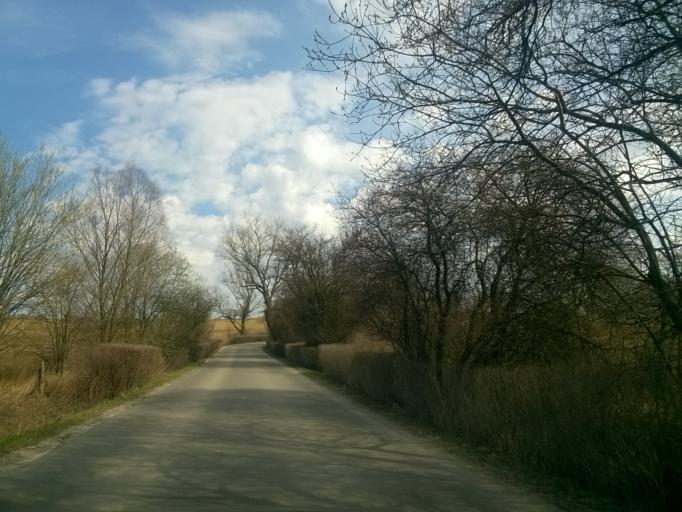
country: PL
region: Lesser Poland Voivodeship
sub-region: Powiat krakowski
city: Rzaska
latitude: 50.0874
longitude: 19.8532
